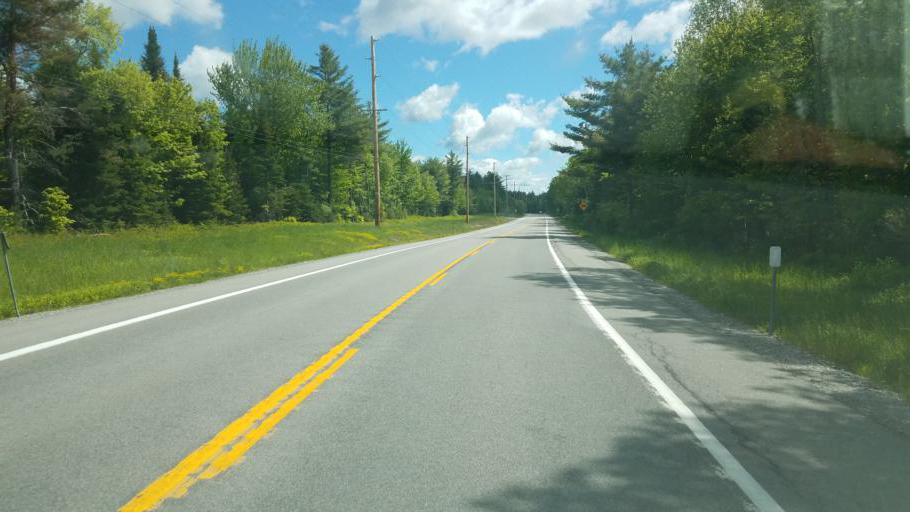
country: US
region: New York
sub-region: Oneida County
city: Boonville
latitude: 43.4927
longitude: -75.1592
